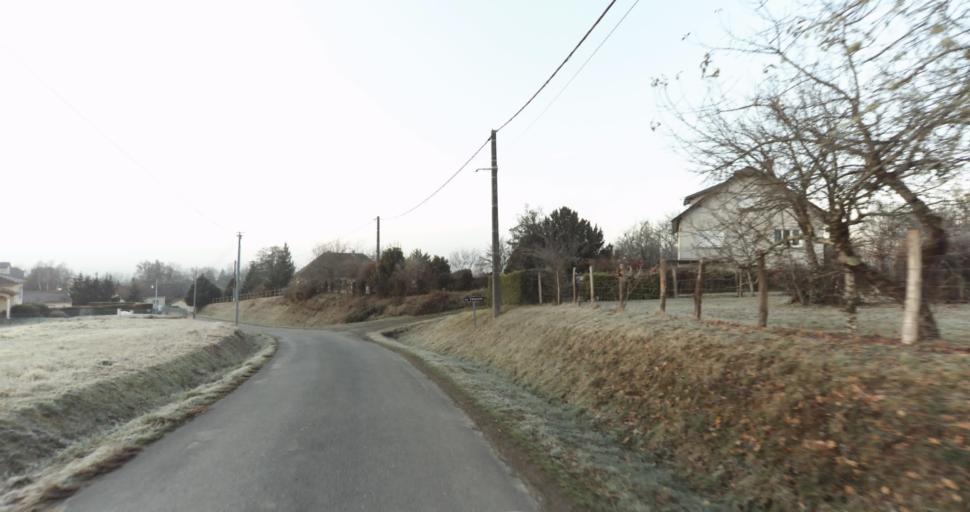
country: FR
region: Limousin
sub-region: Departement de la Haute-Vienne
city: Aixe-sur-Vienne
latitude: 45.8041
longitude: 1.1274
